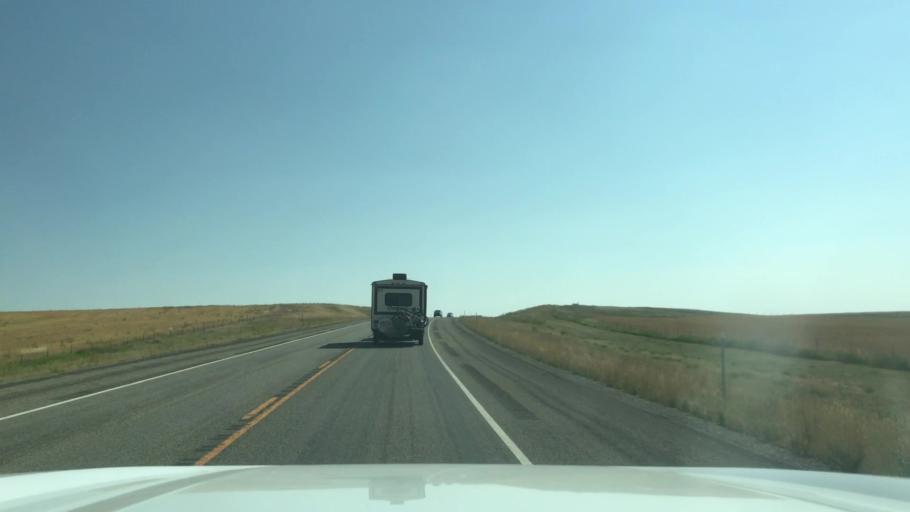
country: US
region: Montana
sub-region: Wheatland County
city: Harlowton
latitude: 46.4714
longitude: -109.7667
